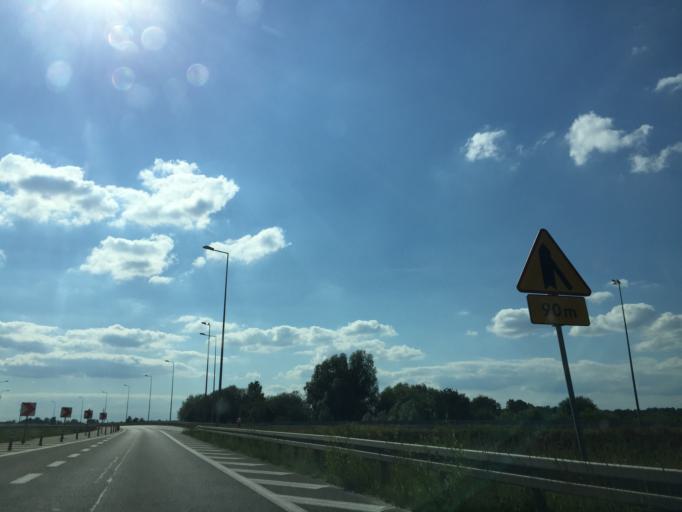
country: PL
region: Warmian-Masurian Voivodeship
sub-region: Powiat elcki
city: Elk
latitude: 53.8417
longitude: 22.3410
